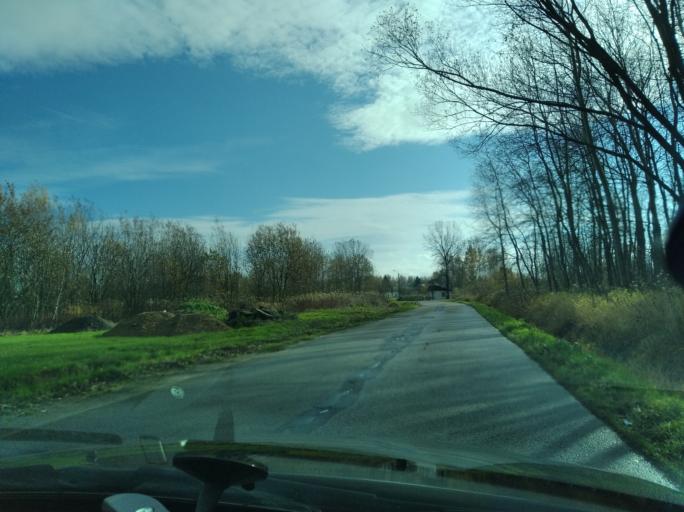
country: PL
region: Subcarpathian Voivodeship
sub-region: Powiat ropczycko-sedziszowski
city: Ostrow
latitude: 50.0869
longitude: 21.5731
